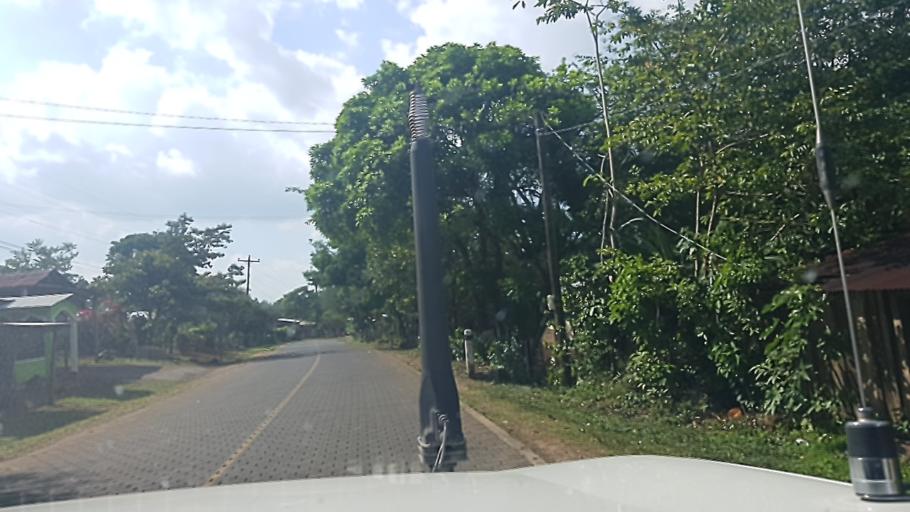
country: NI
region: Atlantico Sur
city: Nueva Guinea
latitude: 11.7019
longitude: -84.3763
